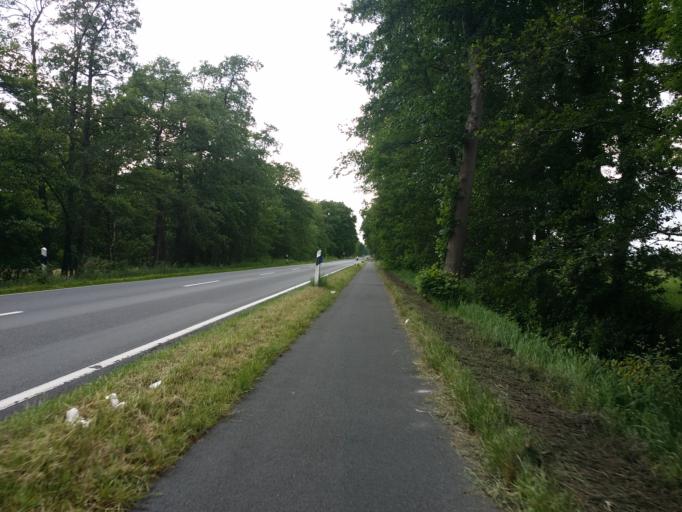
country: DE
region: Lower Saxony
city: Friedeburg
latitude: 53.4979
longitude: 7.8235
